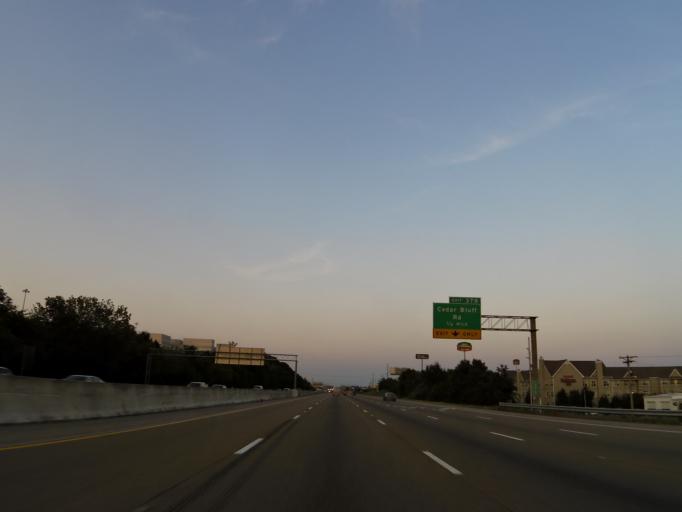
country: US
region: Tennessee
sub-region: Knox County
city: Farragut
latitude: 35.9148
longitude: -84.1055
